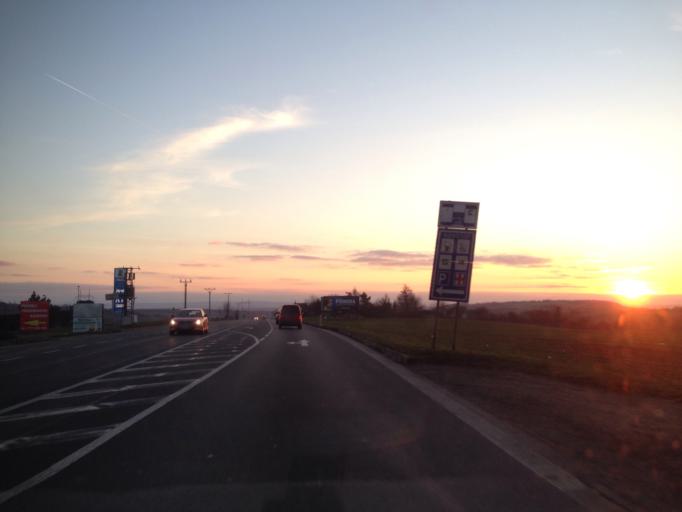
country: CZ
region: Central Bohemia
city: Revnicov
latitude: 50.1824
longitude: 13.8003
